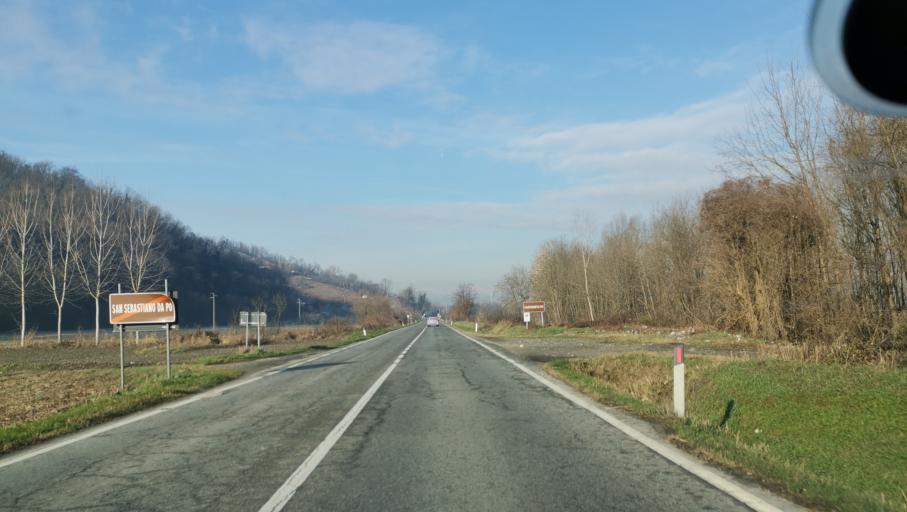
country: IT
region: Piedmont
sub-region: Provincia di Torino
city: San Sebastiano da Po
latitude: 45.1729
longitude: 7.9261
